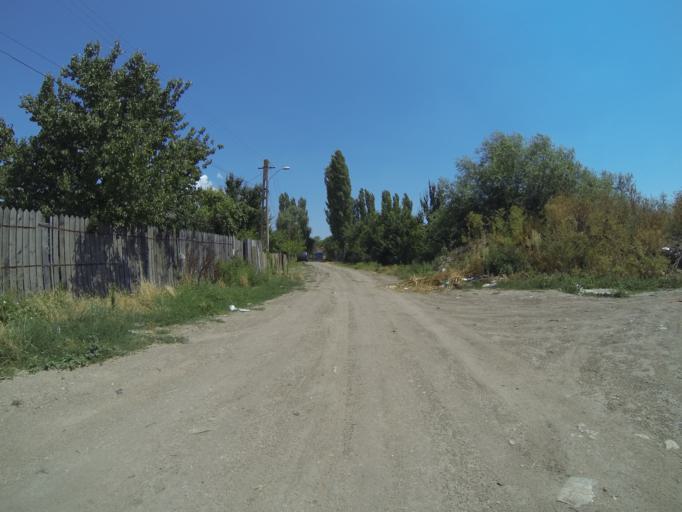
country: RO
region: Dolj
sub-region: Comuna Segarcea
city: Segarcea
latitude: 44.0896
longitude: 23.7367
